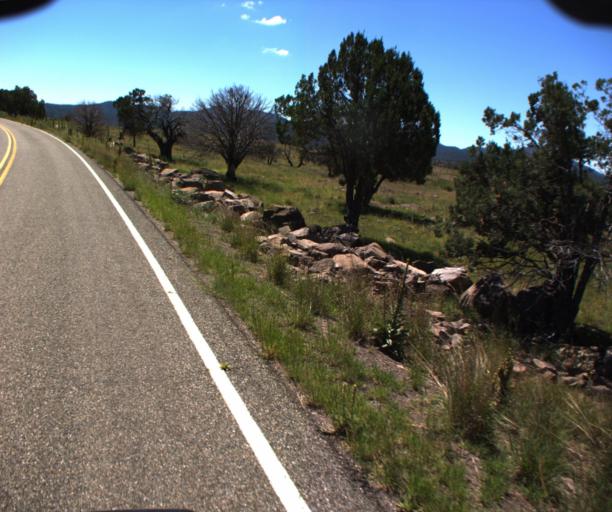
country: US
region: Arizona
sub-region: Greenlee County
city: Morenci
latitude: 33.2957
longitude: -109.3609
